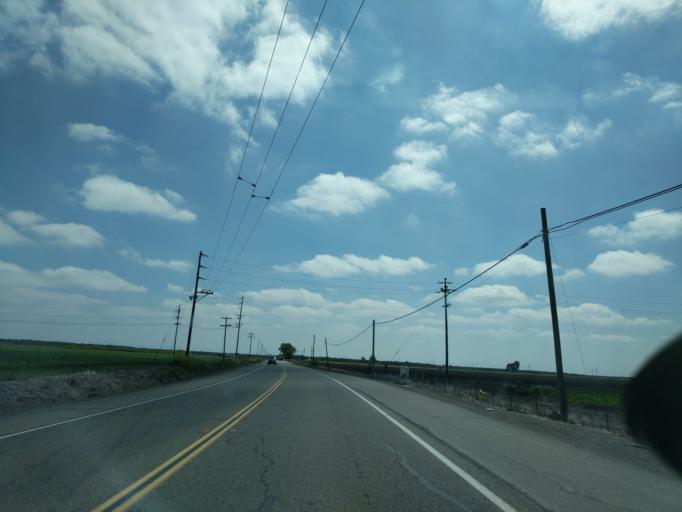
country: US
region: California
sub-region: San Joaquin County
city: Garden Acres
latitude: 37.9491
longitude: -121.1808
